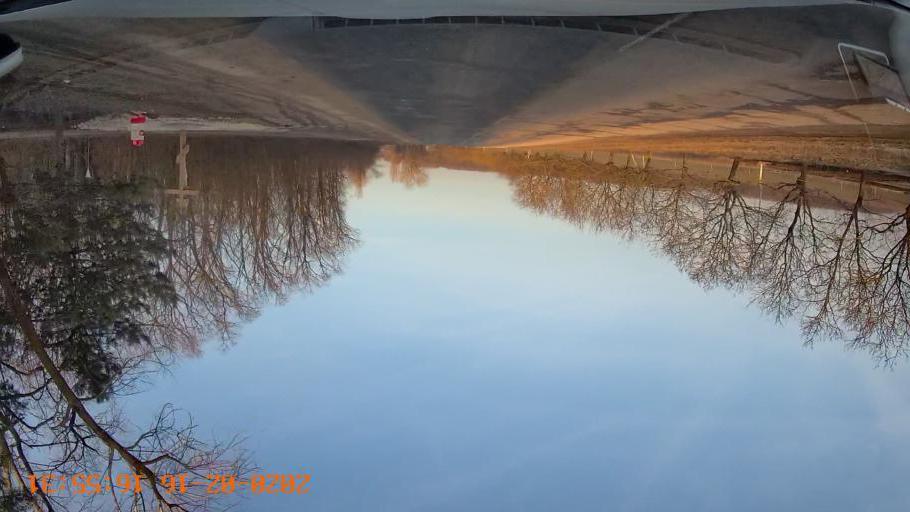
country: MD
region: Briceni
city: Briceni
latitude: 48.3281
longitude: 27.0307
